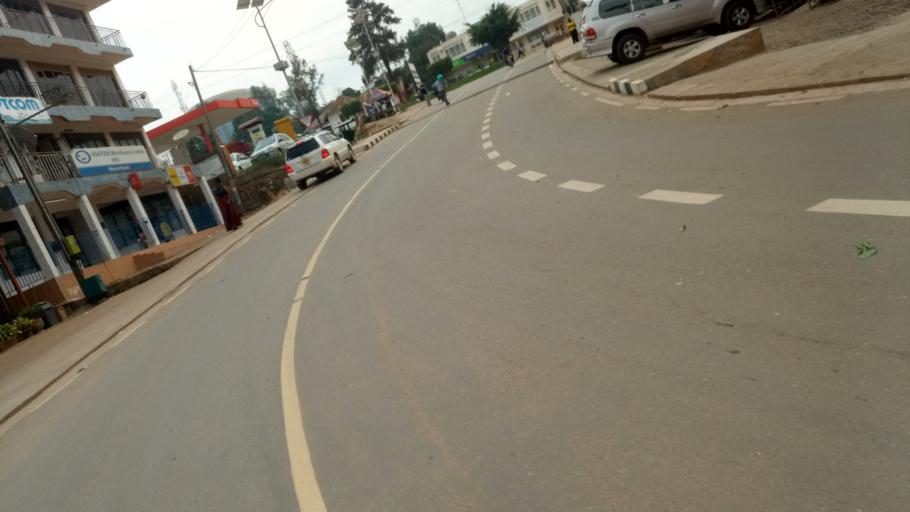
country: UG
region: Western Region
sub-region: Mbarara District
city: Mbarara
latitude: -0.6092
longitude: 30.6614
